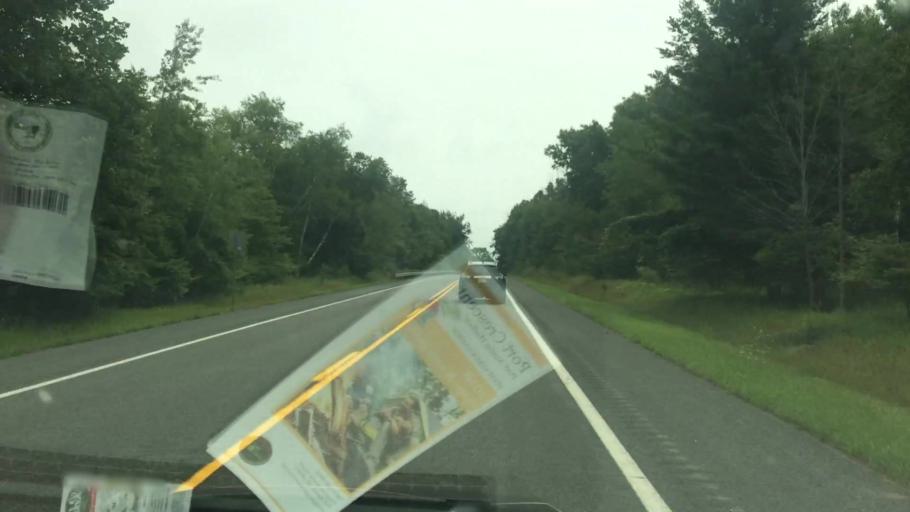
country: US
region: Michigan
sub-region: Huron County
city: Harbor Beach
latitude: 44.0248
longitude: -82.8204
